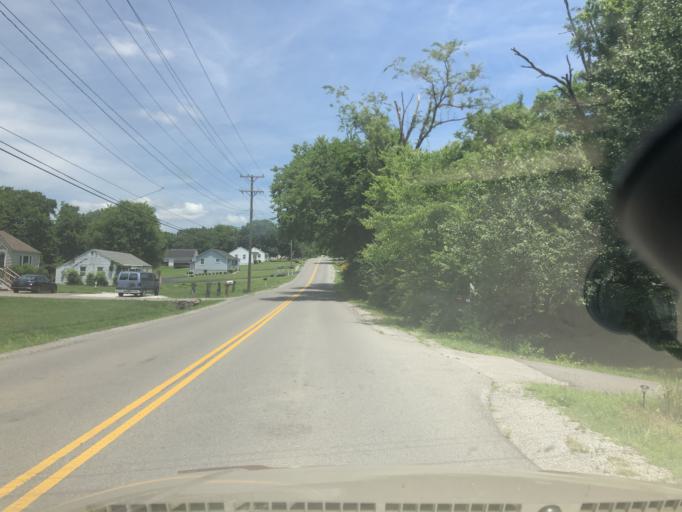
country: US
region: Tennessee
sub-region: Davidson County
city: Lakewood
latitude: 36.2543
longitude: -86.6932
